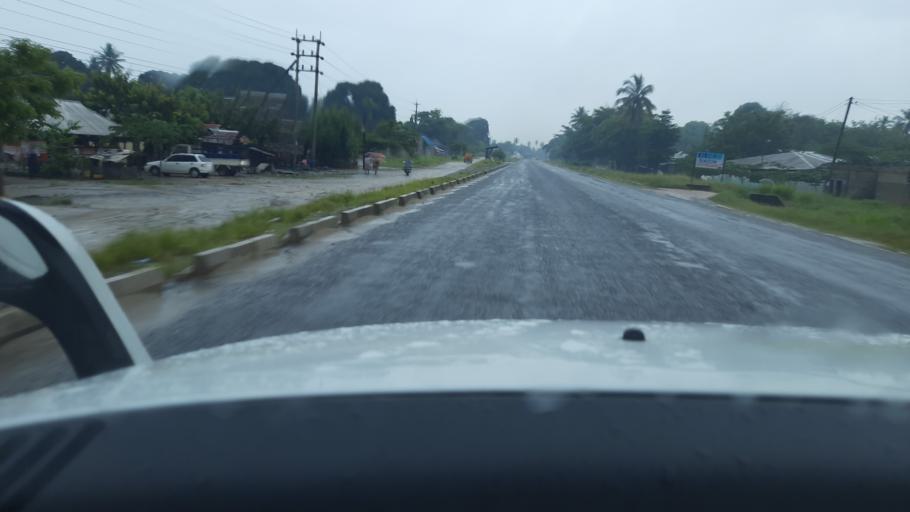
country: TZ
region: Pwani
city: Bagamoyo
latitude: -6.5102
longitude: 38.9364
